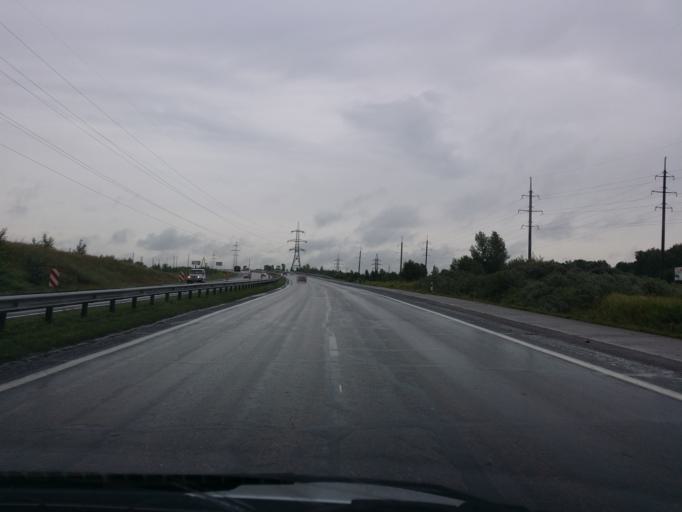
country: RU
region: Altai Krai
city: Sannikovo
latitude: 53.3463
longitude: 83.9441
